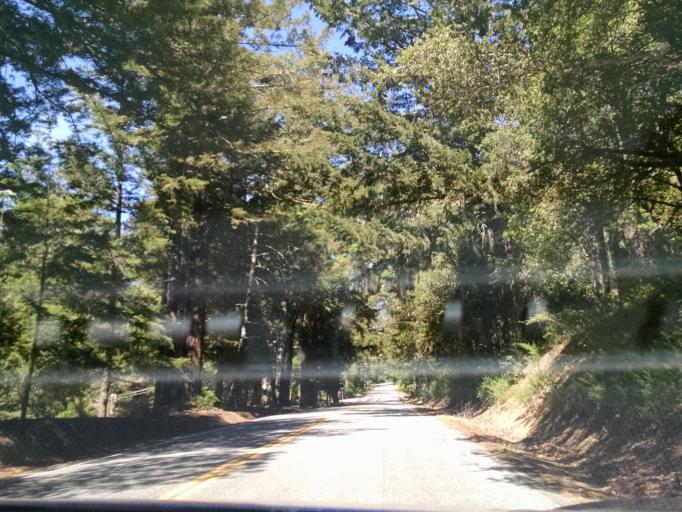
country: US
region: California
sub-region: San Mateo County
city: Portola Valley
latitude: 37.3878
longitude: -122.2663
